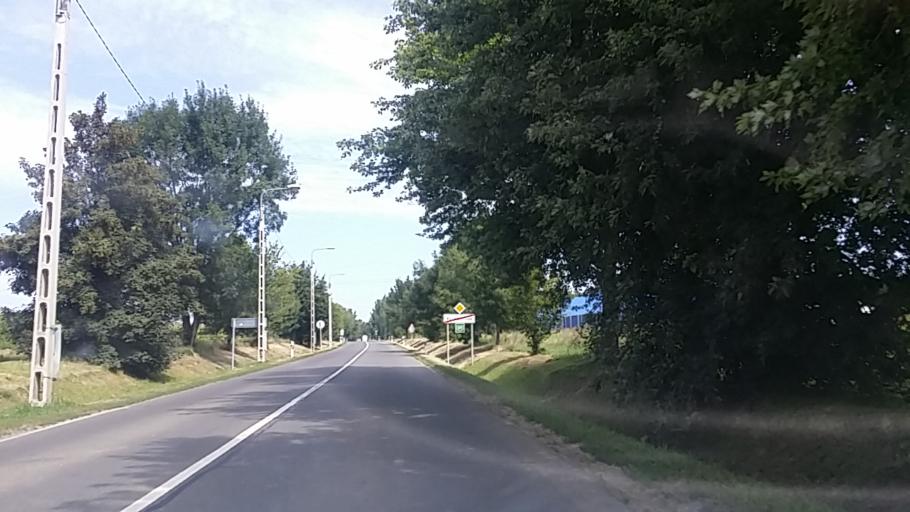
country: HU
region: Baranya
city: Sasd
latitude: 46.3122
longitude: 18.1320
